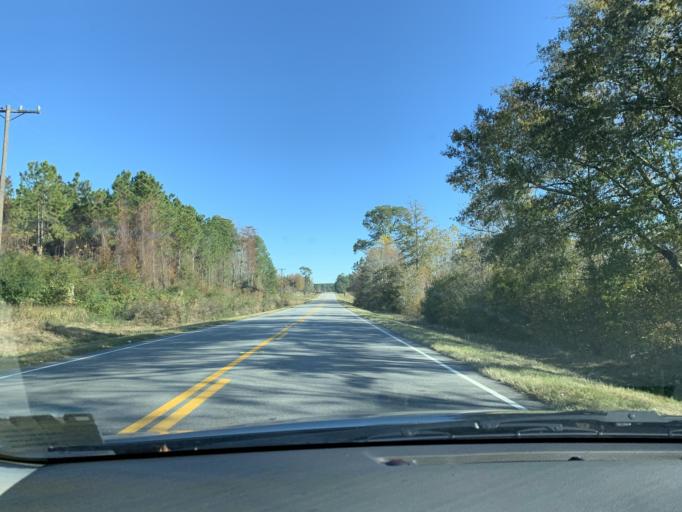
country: US
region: Georgia
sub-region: Ben Hill County
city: Fitzgerald
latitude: 31.7185
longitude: -83.1861
